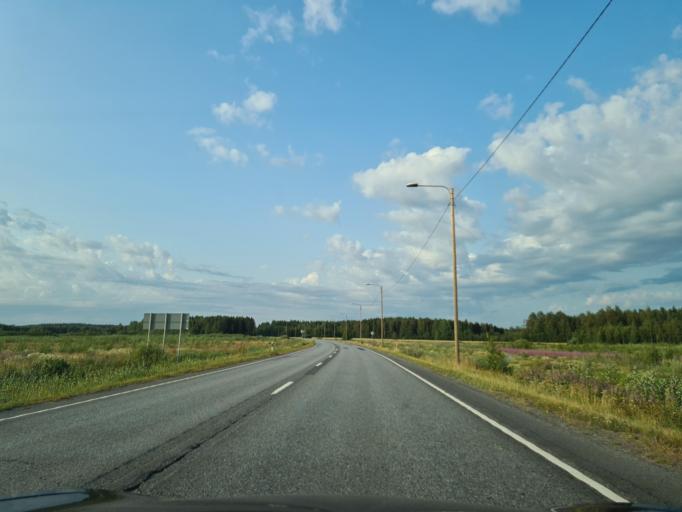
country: FI
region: Southern Ostrobothnia
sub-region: Seinaejoki
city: Kauhava
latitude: 63.0597
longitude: 23.0384
